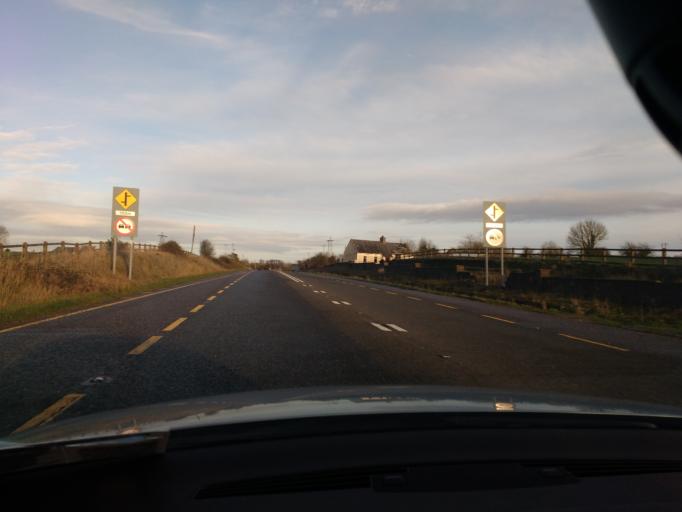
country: IE
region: Munster
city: Thurles
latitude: 52.6472
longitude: -7.7237
